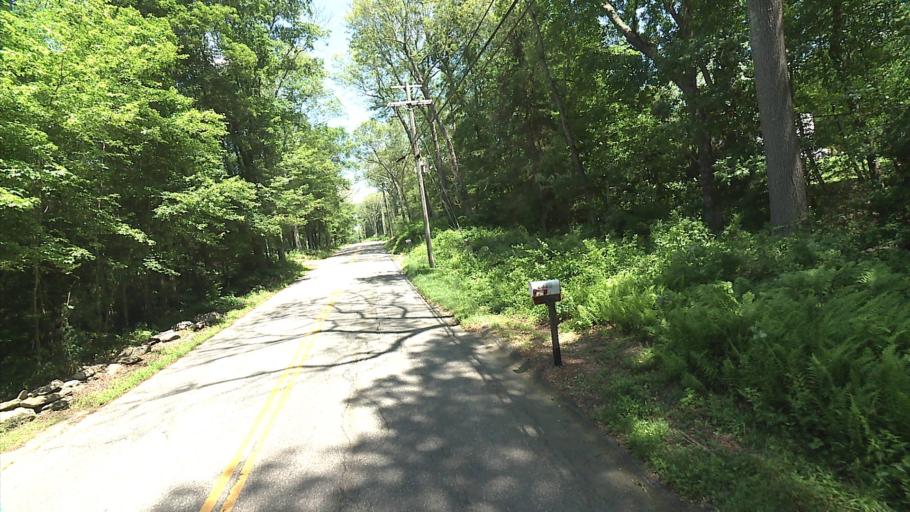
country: US
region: Connecticut
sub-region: New London County
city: Preston City
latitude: 41.5274
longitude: -71.8799
